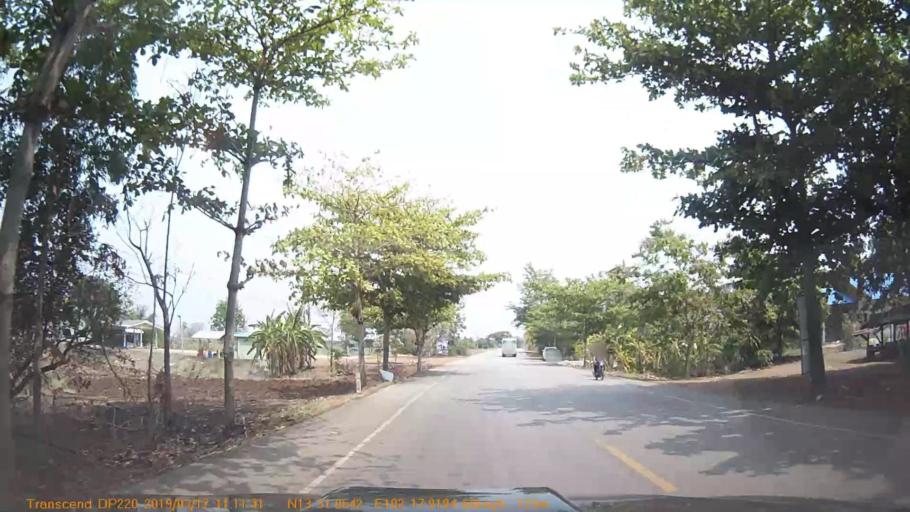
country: TH
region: Sa Kaeo
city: Khlong Hat
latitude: 13.5178
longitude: 102.2987
